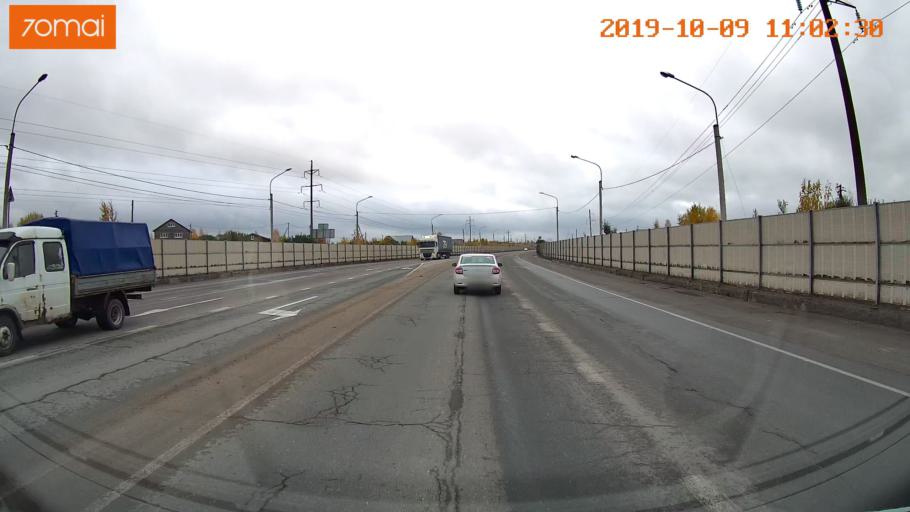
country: RU
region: Vologda
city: Vologda
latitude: 59.2320
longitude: 39.7741
